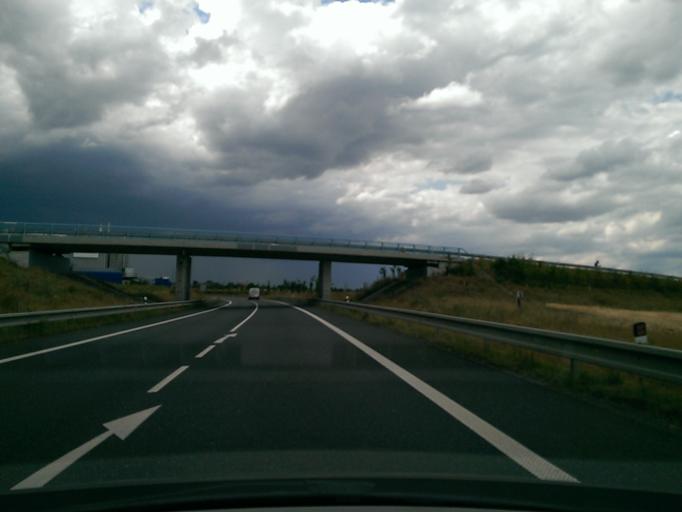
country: CZ
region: Central Bohemia
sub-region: Okres Nymburk
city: Nymburk
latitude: 50.2031
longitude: 15.0466
